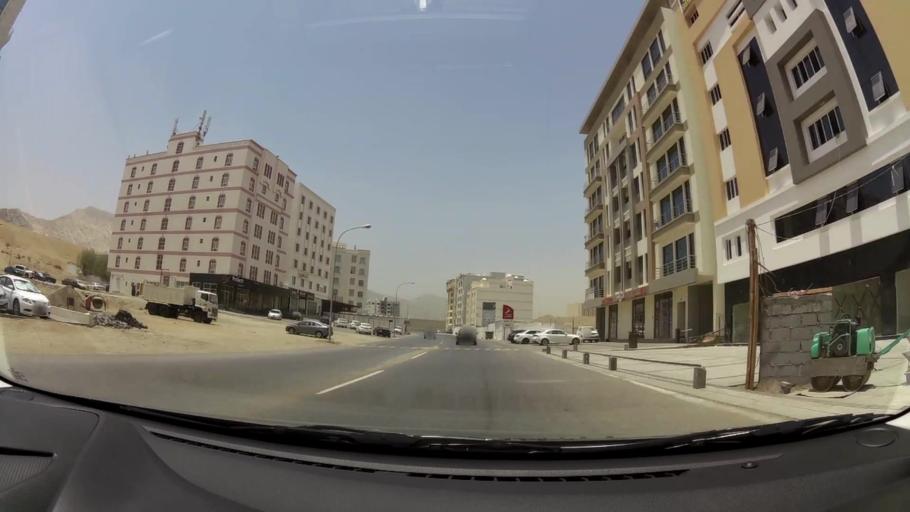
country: OM
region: Muhafazat Masqat
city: Bawshar
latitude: 23.5750
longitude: 58.4168
